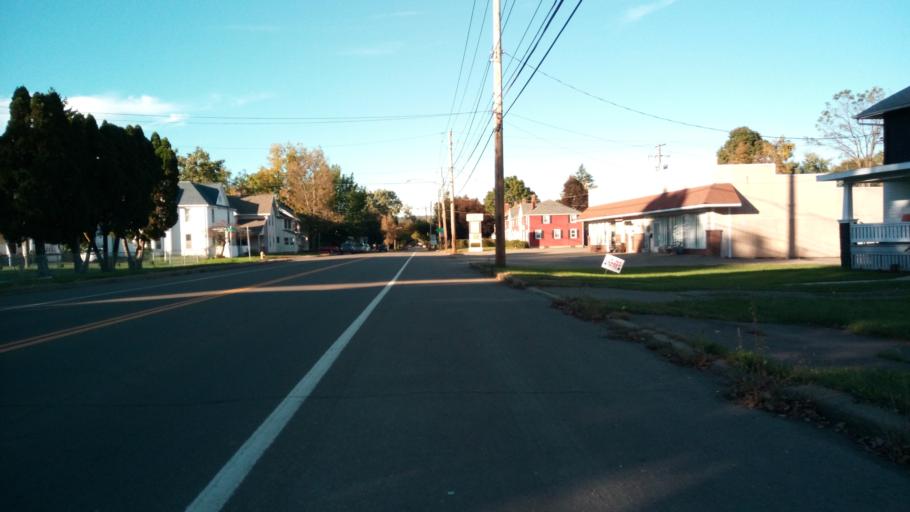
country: US
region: New York
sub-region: Chemung County
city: Southport
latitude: 42.0651
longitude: -76.8079
